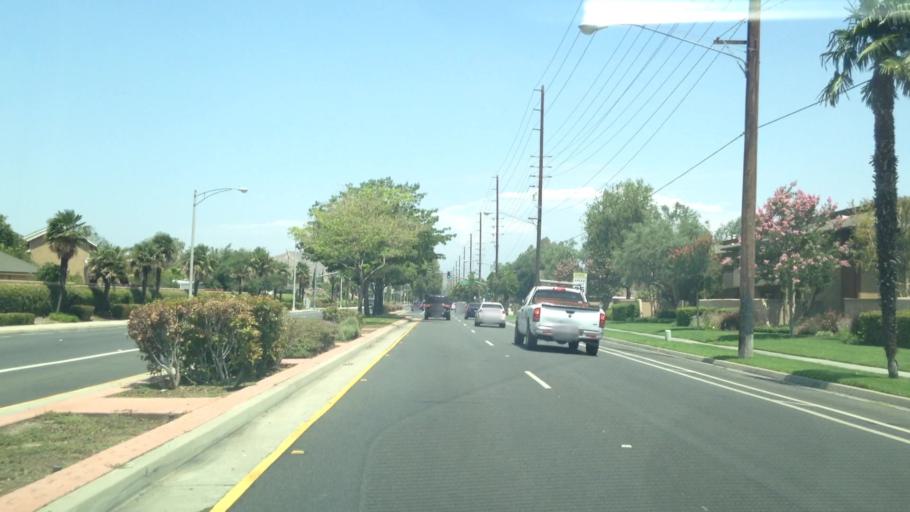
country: US
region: California
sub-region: Riverside County
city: Home Gardens
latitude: 33.9057
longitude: -117.4780
